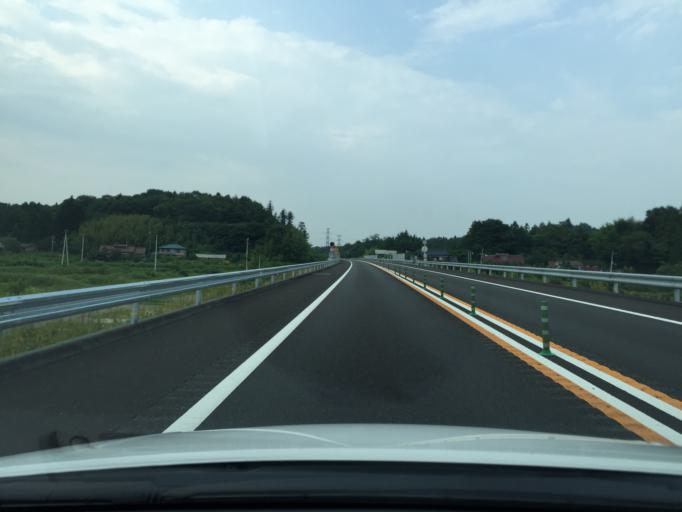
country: JP
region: Fukushima
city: Namie
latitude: 37.5164
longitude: 140.9441
